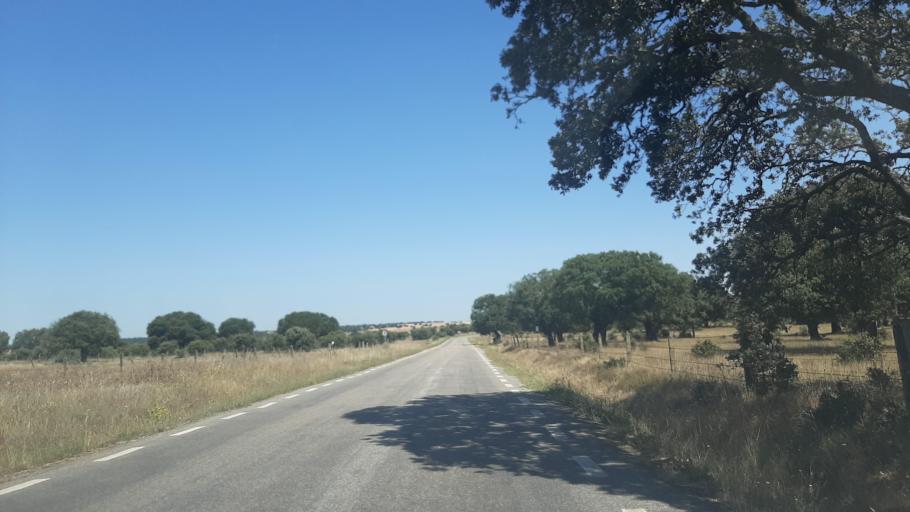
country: ES
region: Castille and Leon
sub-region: Provincia de Salamanca
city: Cabrillas
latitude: 40.7287
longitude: -6.1767
